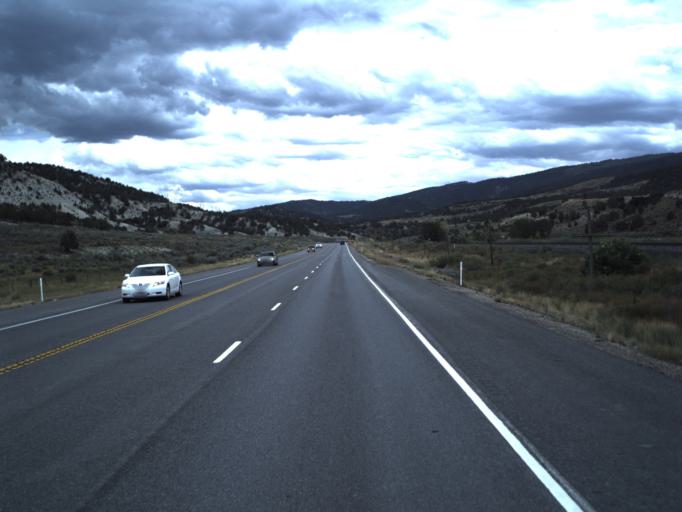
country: US
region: Utah
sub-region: Utah County
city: Mapleton
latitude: 39.9724
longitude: -111.3353
